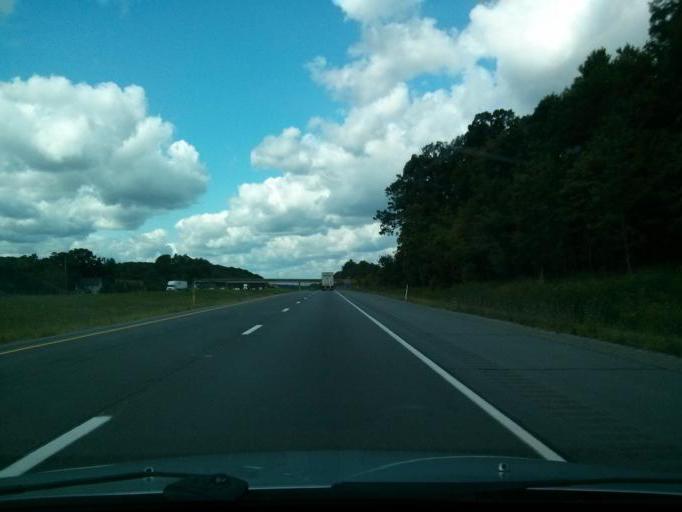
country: US
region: Pennsylvania
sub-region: Clearfield County
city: Treasure Lake
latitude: 41.1214
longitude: -78.6481
